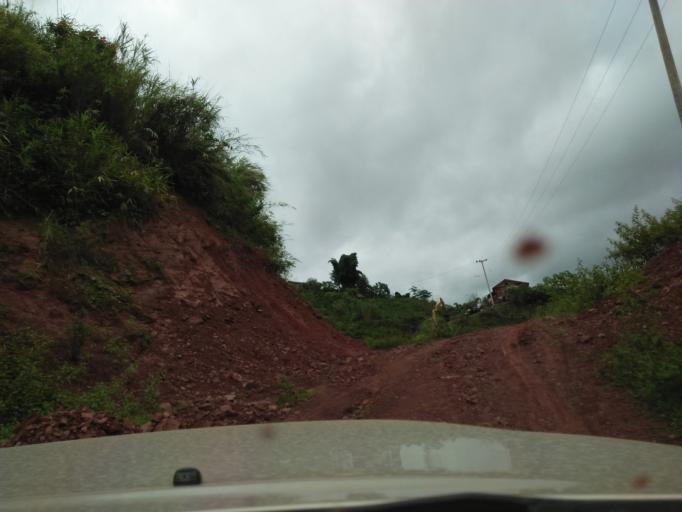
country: TH
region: Nan
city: Bo Kluea
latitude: 19.3803
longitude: 101.2075
